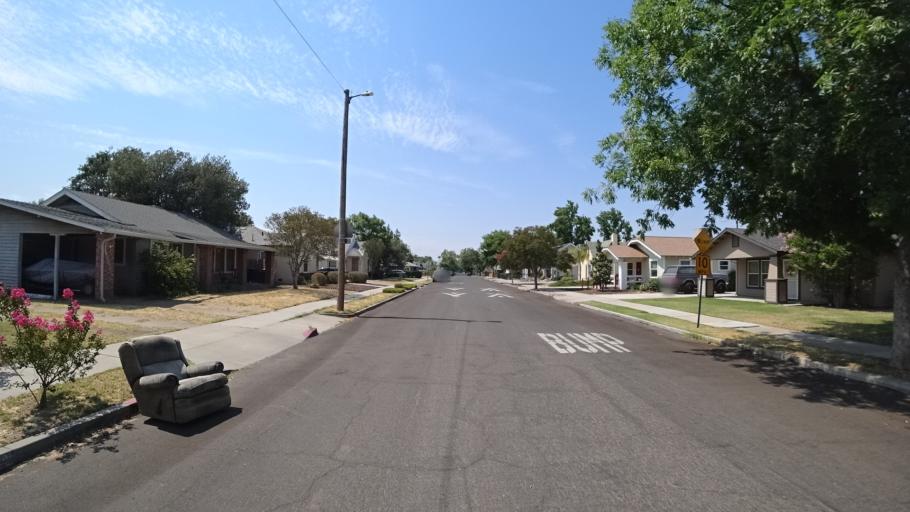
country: US
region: California
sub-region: Fresno County
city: Fresno
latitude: 36.7622
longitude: -119.7945
